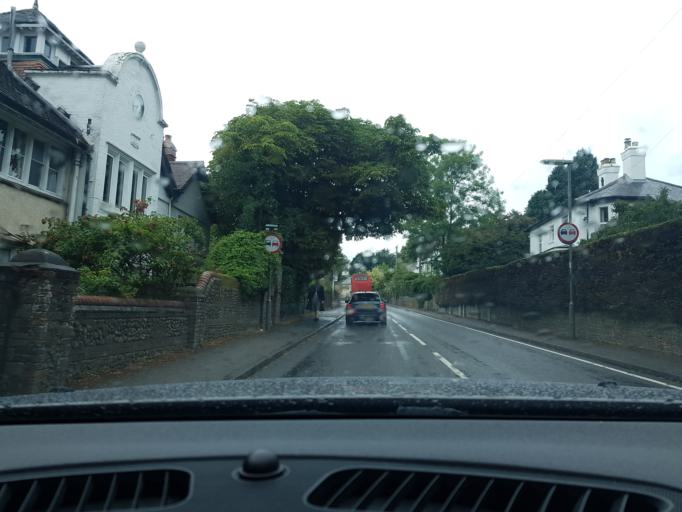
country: GB
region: England
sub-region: Surrey
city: Hale
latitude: 51.2331
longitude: -0.7927
